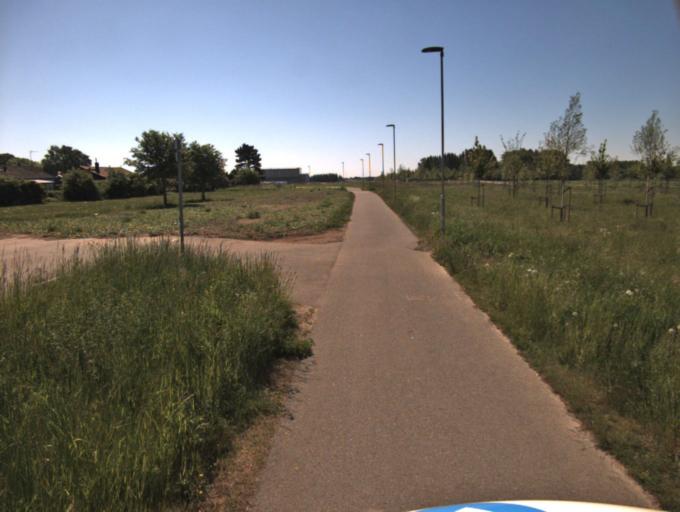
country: SE
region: Skane
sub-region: Kristianstads Kommun
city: Kristianstad
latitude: 56.0281
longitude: 14.1900
